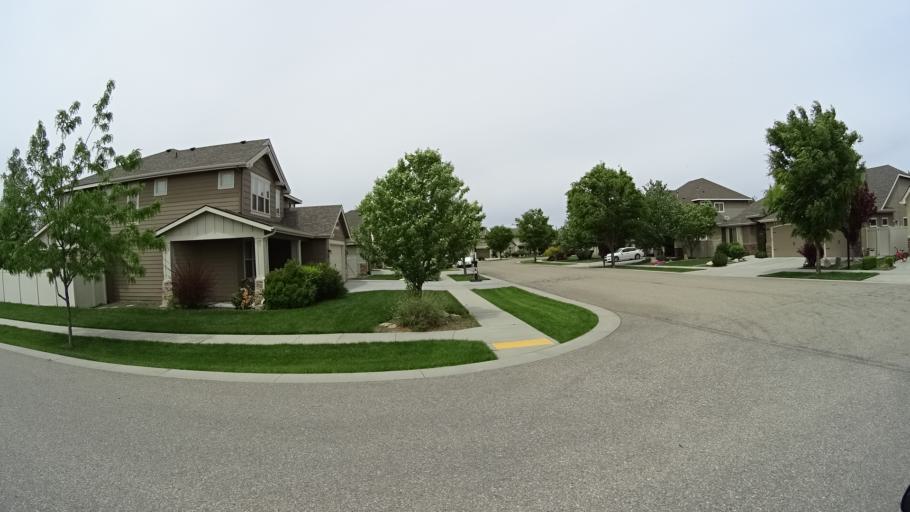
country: US
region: Idaho
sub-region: Ada County
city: Meridian
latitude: 43.5646
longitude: -116.3626
